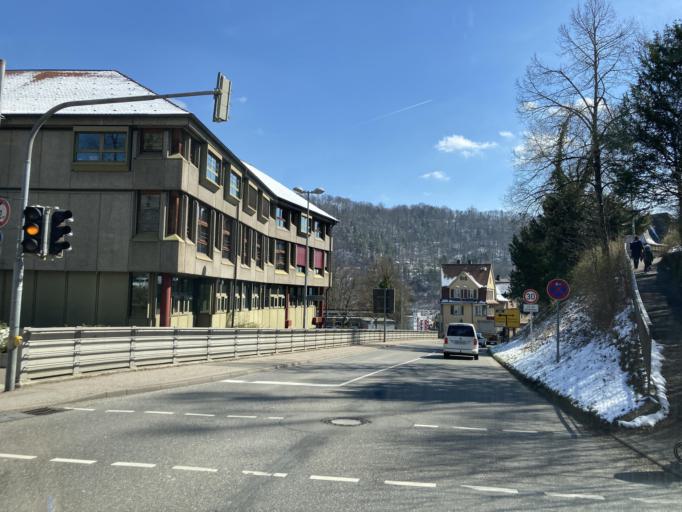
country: DE
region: Baden-Wuerttemberg
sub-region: Freiburg Region
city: Oberndorf
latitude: 48.2906
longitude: 8.5727
